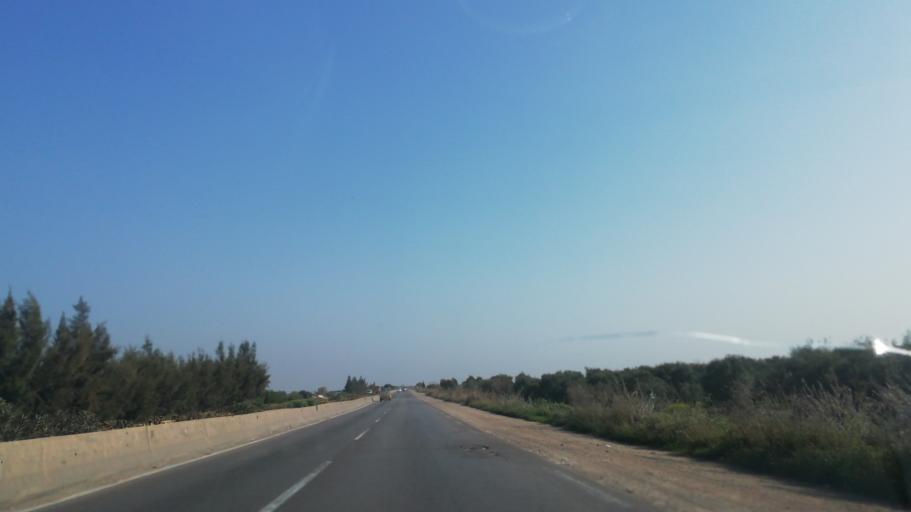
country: DZ
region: Oran
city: Bou Tlelis
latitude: 35.5670
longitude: -0.8942
